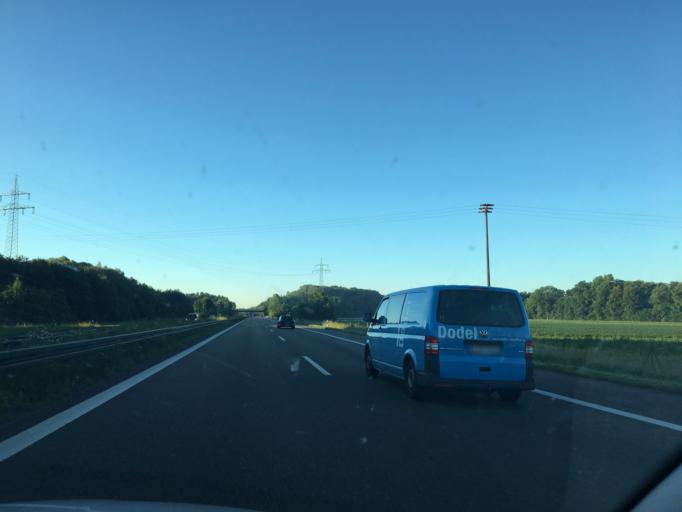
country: DE
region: Bavaria
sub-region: Swabia
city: Neu-Ulm
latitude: 48.3569
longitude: 10.0093
